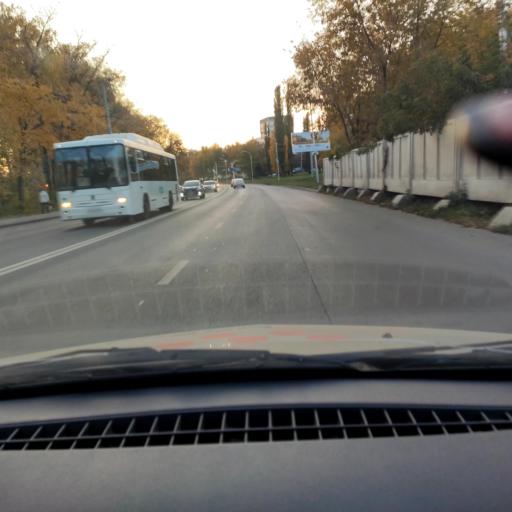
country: RU
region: Bashkortostan
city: Ufa
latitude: 54.8116
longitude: 56.0739
